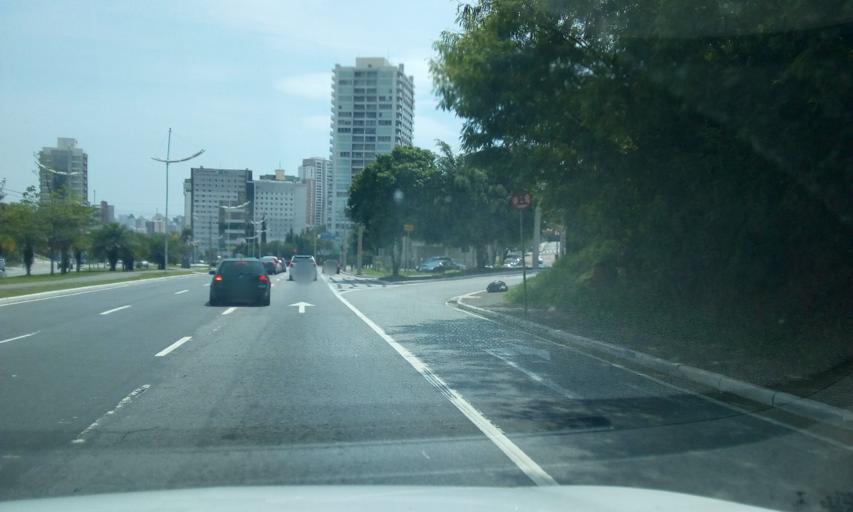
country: BR
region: Sao Paulo
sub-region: Jundiai
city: Jundiai
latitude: -23.2050
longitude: -46.8936
